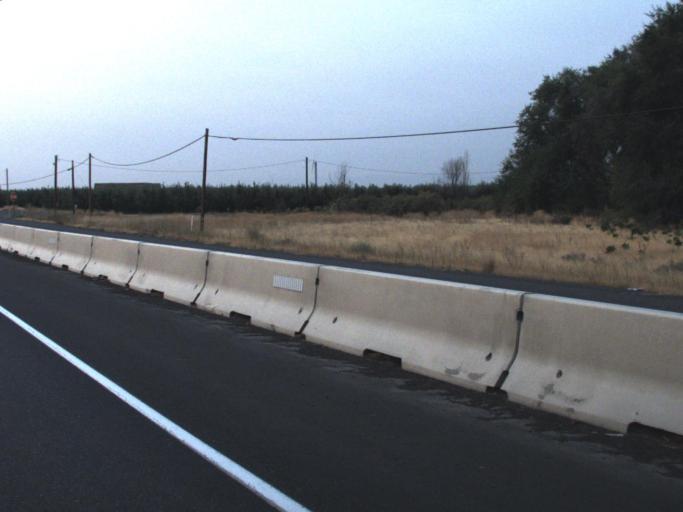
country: US
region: Washington
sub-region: Yakima County
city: Wapato
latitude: 46.4784
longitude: -120.4476
